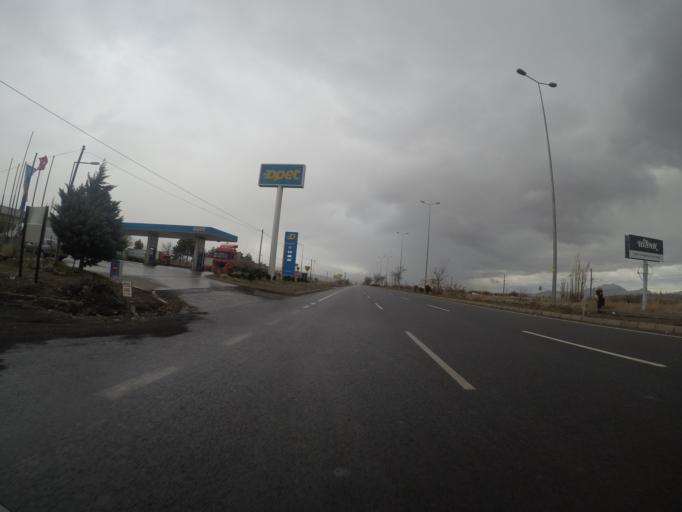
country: TR
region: Kayseri
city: Incesu
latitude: 38.6907
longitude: 35.2429
